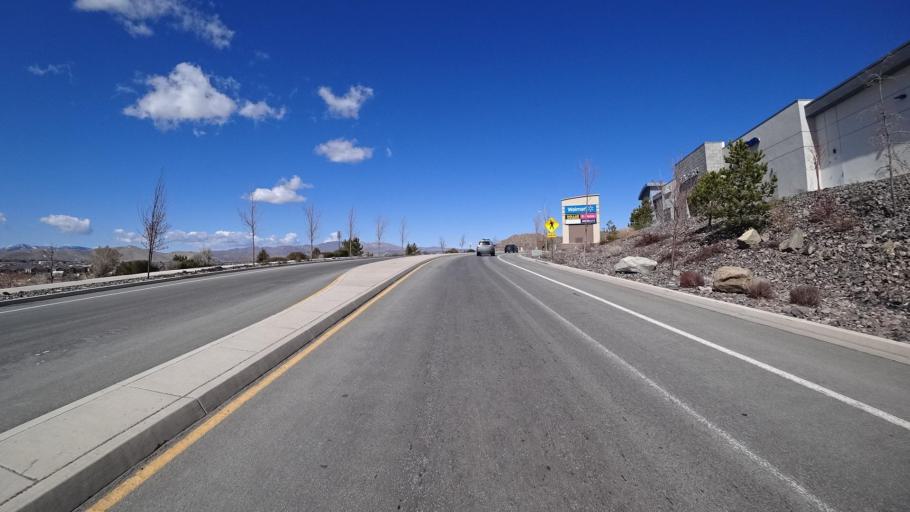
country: US
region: Nevada
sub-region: Washoe County
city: Lemmon Valley
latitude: 39.6157
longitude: -119.8552
